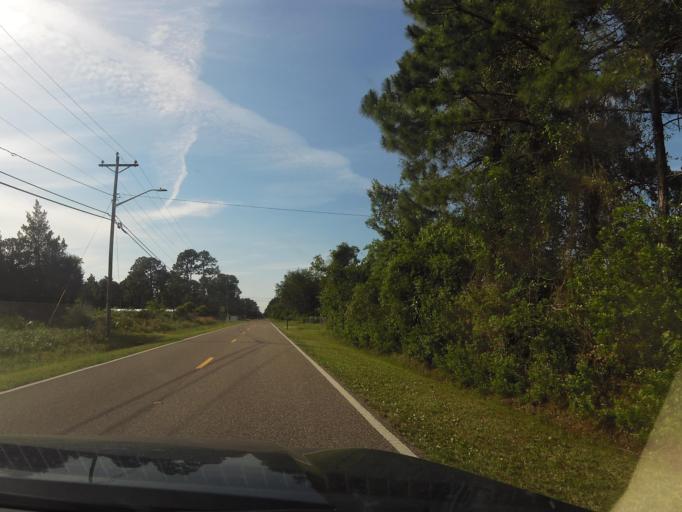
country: US
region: Florida
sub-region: Nassau County
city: Fernandina Beach
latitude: 30.5164
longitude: -81.4787
